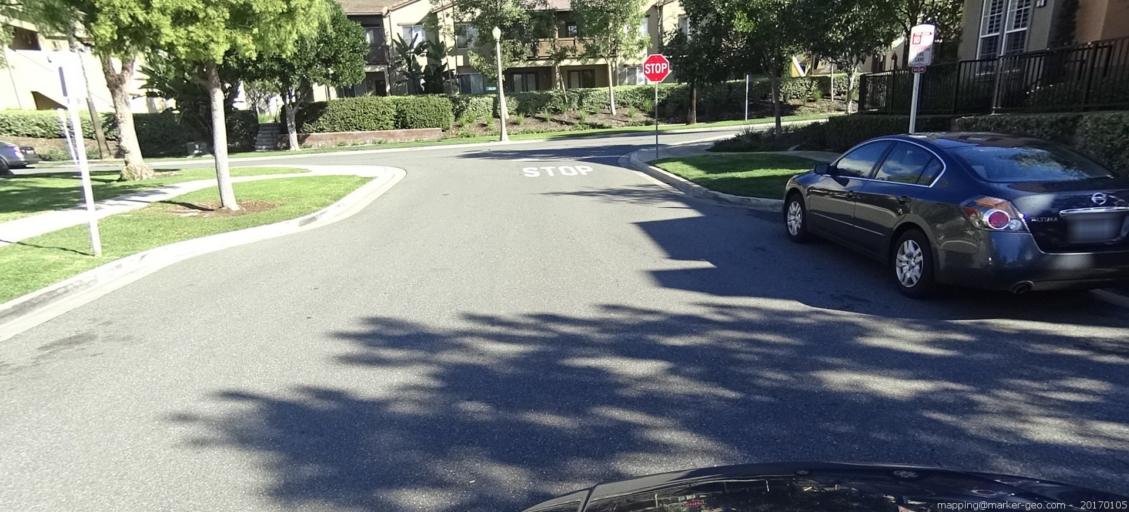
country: US
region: California
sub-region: Orange County
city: Ladera Ranch
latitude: 33.5528
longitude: -117.6330
